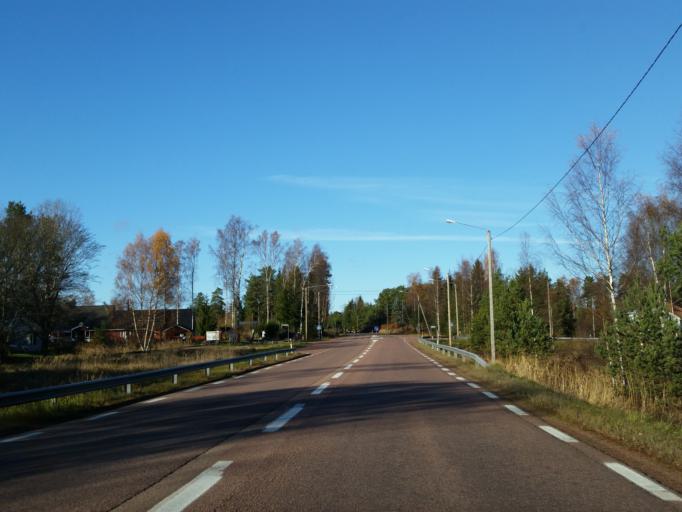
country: AX
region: Alands landsbygd
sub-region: Finstroem
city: Finstroem
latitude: 60.2334
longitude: 19.9824
